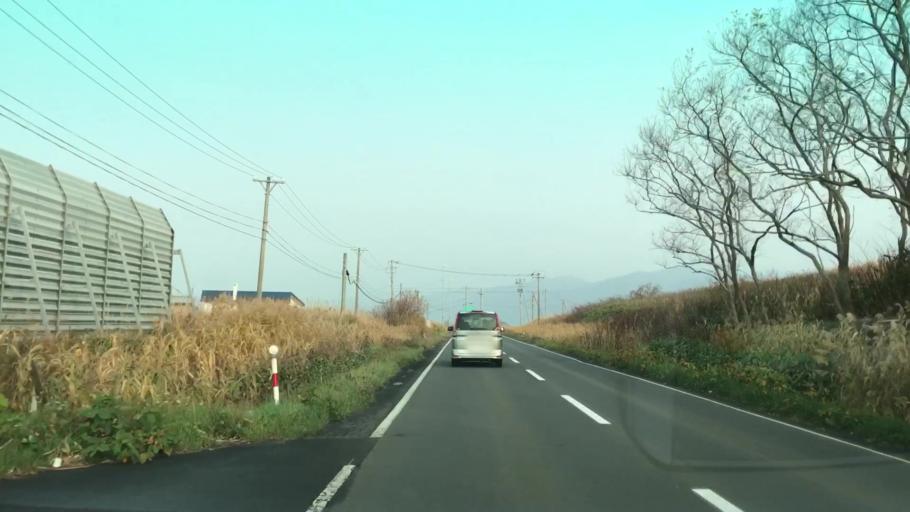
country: JP
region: Hokkaido
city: Ishikari
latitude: 43.3694
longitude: 141.4268
